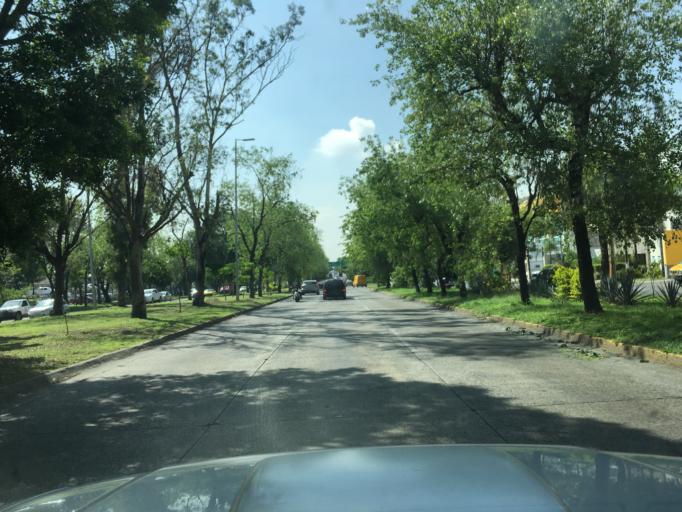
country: MX
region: Jalisco
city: Guadalajara
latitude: 20.6550
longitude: -103.3758
